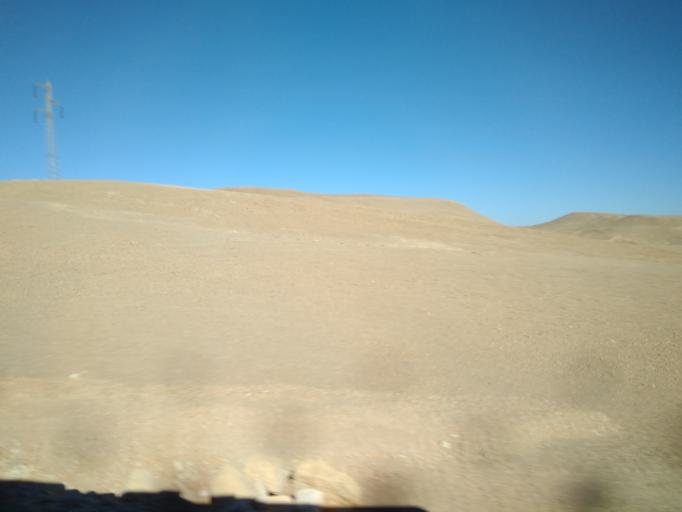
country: IL
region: Southern District
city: Eilat
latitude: 29.6166
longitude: 34.8780
